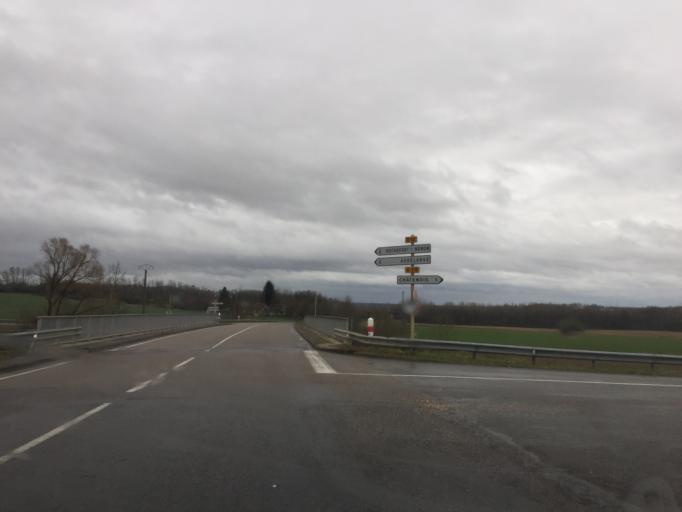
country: FR
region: Franche-Comte
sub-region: Departement du Jura
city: Dole
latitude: 47.1449
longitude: 5.5650
